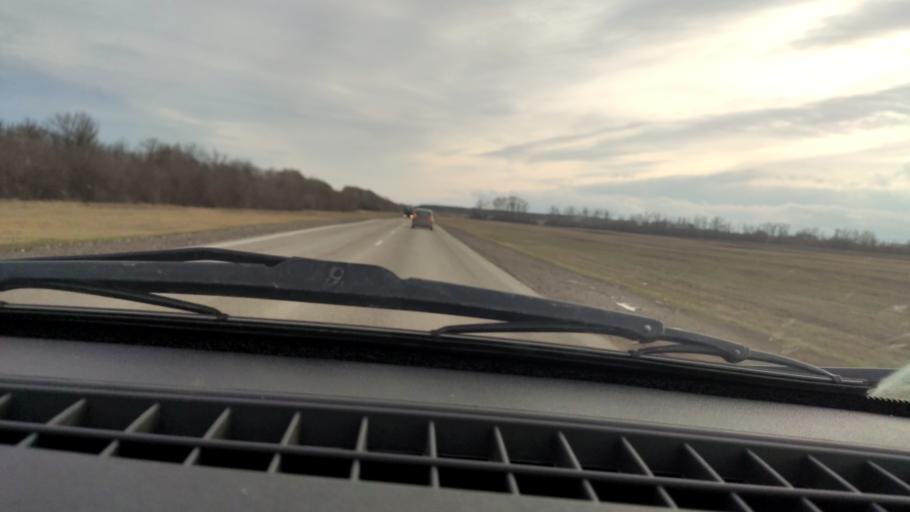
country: RU
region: Bashkortostan
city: Davlekanovo
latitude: 54.2647
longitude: 55.0939
